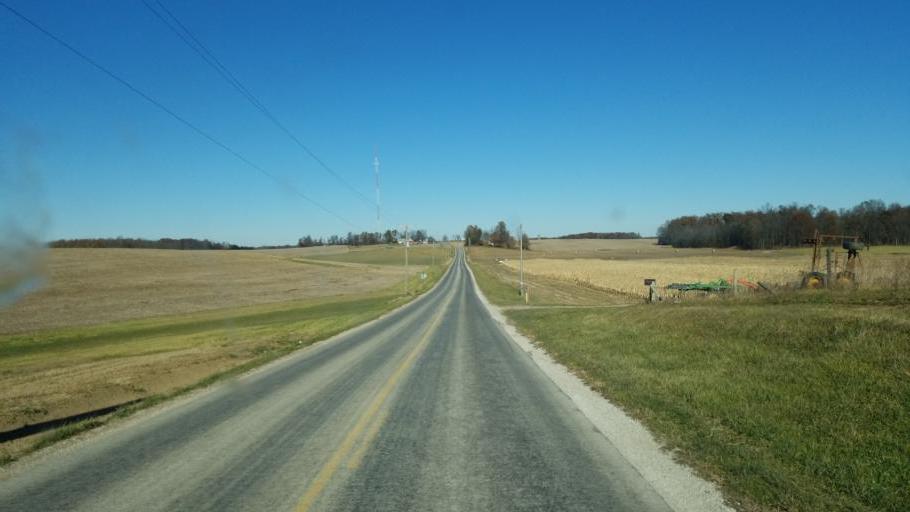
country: US
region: Ohio
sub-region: Huron County
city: Plymouth
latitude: 40.9537
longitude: -82.6196
